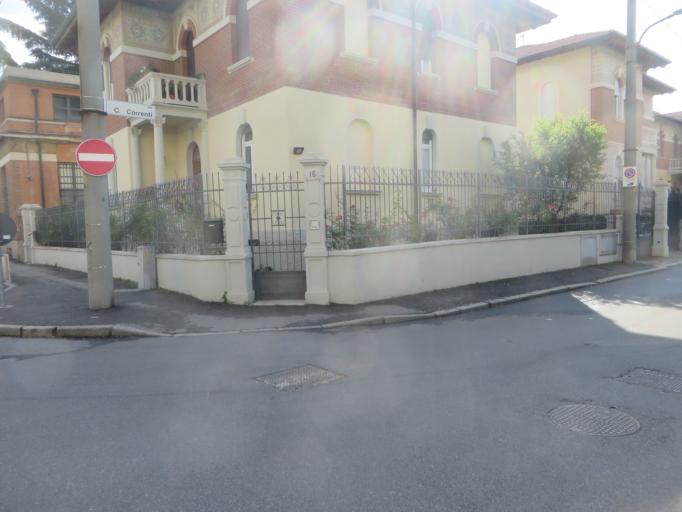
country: IT
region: Lombardy
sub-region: Provincia di Brescia
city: Brescia
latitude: 45.5514
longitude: 10.2207
